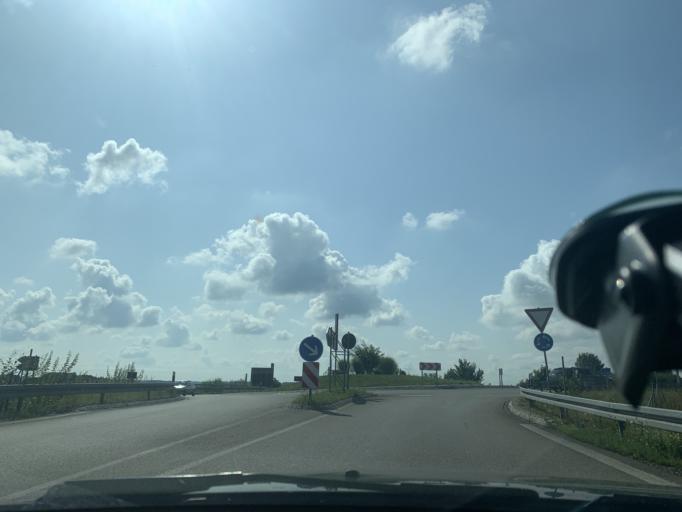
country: DE
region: Bavaria
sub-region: Upper Bavaria
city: Odelzhausen
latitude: 48.3085
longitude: 11.2089
